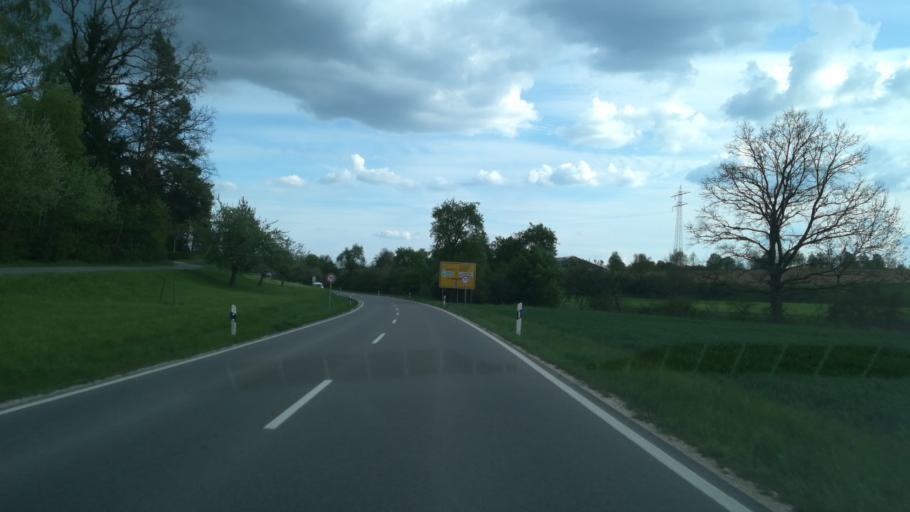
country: DE
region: Baden-Wuerttemberg
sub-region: Tuebingen Region
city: Messkirch
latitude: 48.0078
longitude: 9.1148
